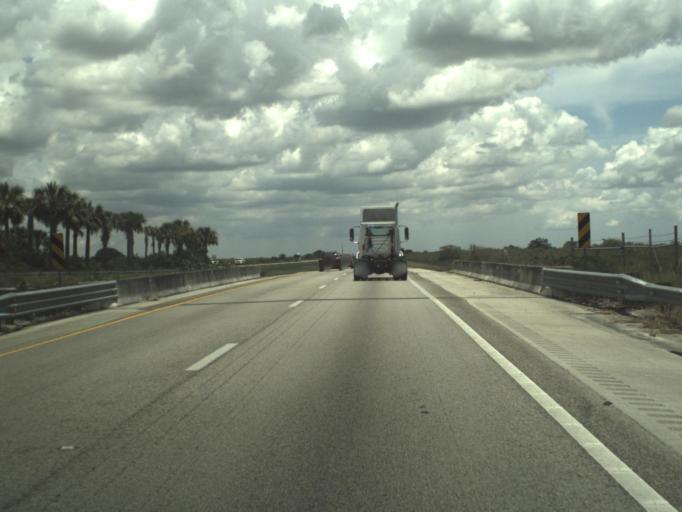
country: US
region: Florida
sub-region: Broward County
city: Weston
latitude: 26.1462
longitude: -80.5953
